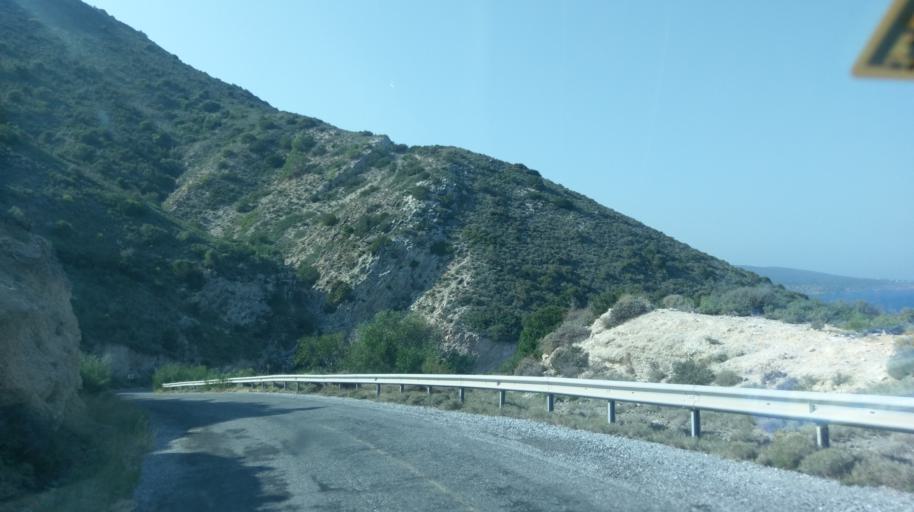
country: CY
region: Keryneia
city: Lapithos
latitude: 35.3656
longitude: 33.0181
